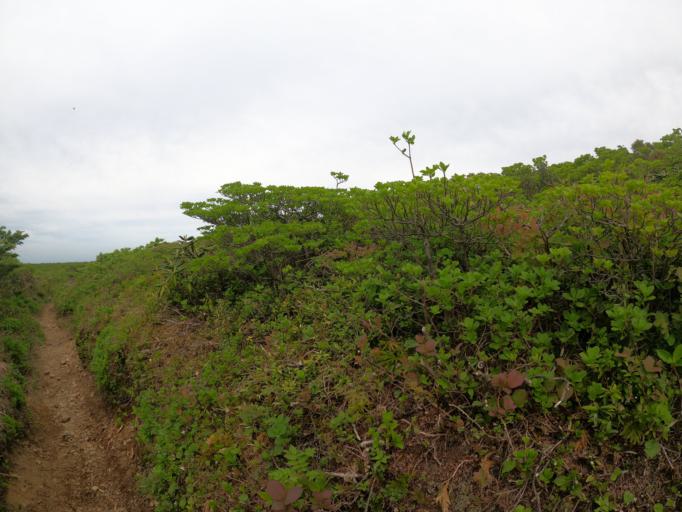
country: JP
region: Iwate
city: Ichinoseki
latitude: 38.9633
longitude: 140.7924
